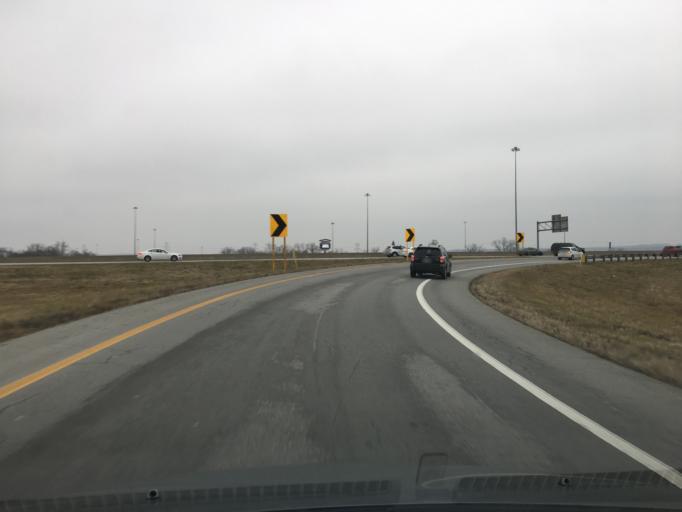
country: US
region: Ohio
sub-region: Hamilton County
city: Glendale
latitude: 39.2900
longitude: -84.4442
